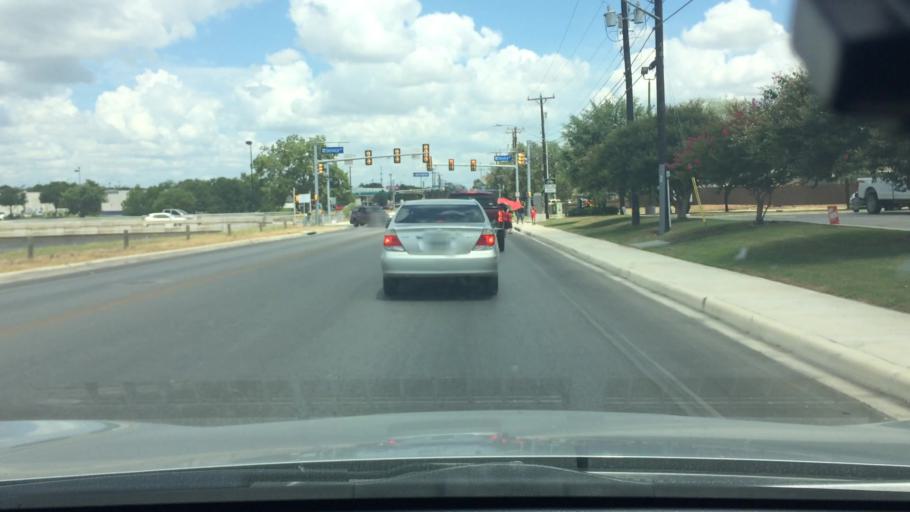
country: US
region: Texas
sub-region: Bexar County
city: China Grove
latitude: 29.3499
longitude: -98.4298
